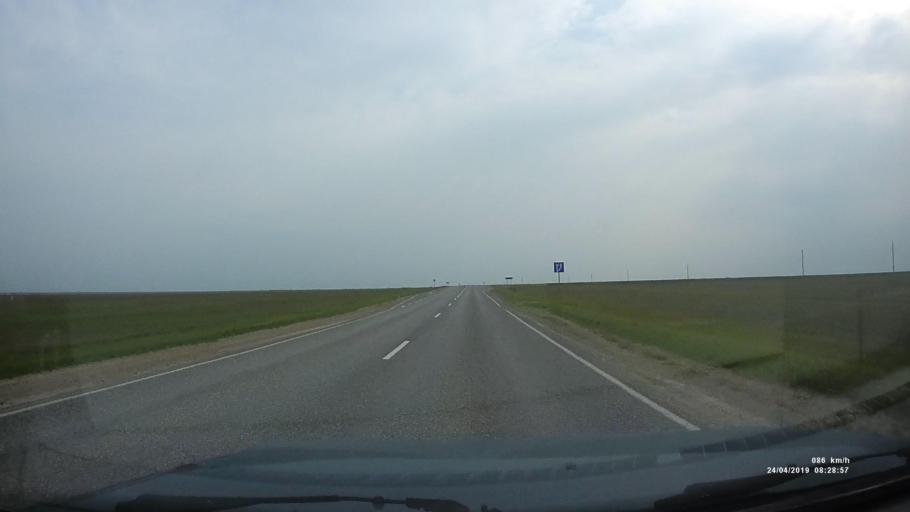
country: RU
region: Kalmykiya
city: Priyutnoye
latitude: 46.1484
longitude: 43.8234
